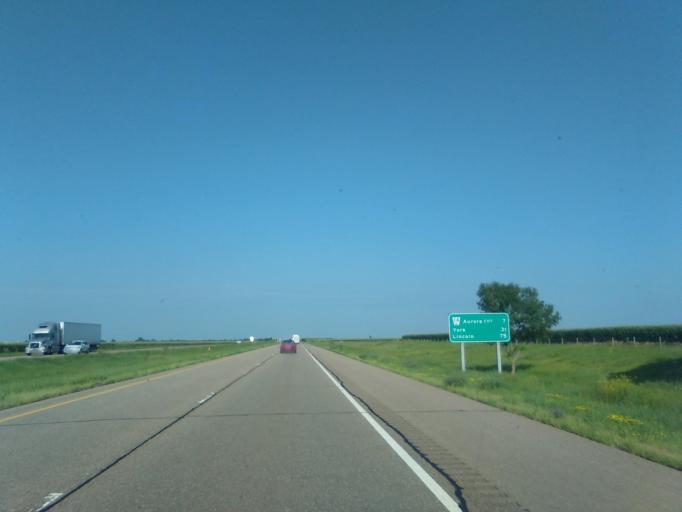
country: US
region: Nebraska
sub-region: Hamilton County
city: Aurora
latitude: 40.8221
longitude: -98.1338
